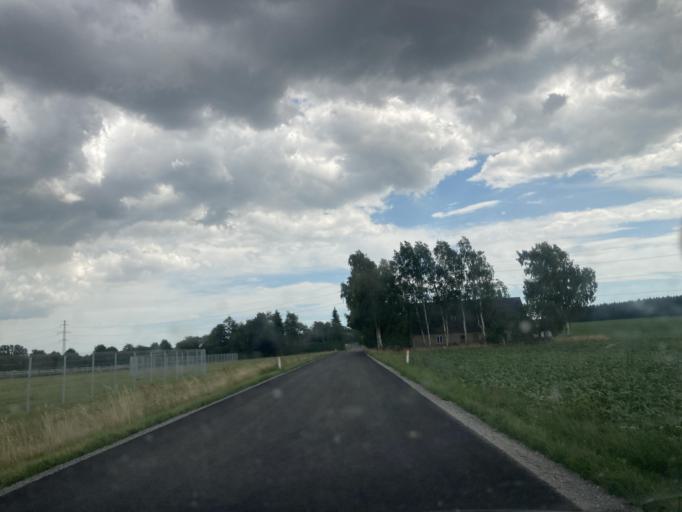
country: DK
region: Zealand
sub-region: Faxe Kommune
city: Haslev
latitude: 55.3317
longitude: 12.0027
